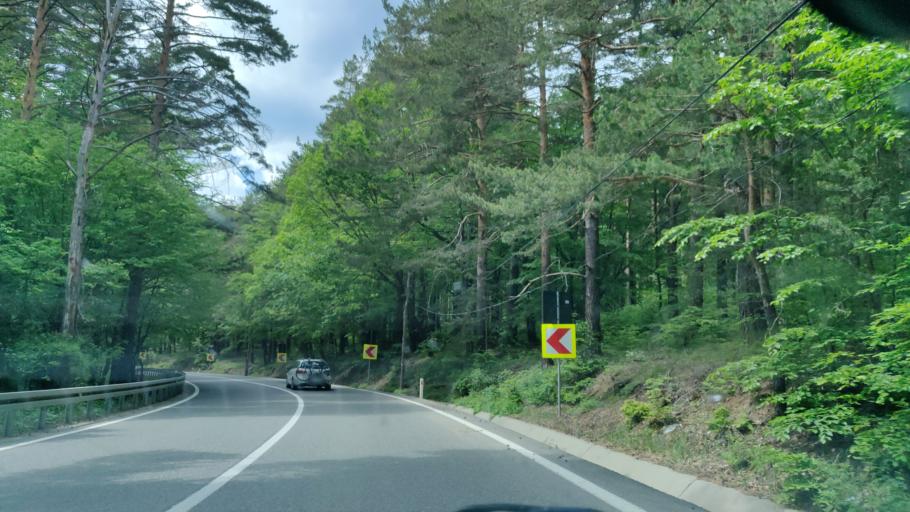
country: RO
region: Vrancea
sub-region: Comuna Tulnici
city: Tulnici
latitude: 45.9221
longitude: 26.6529
